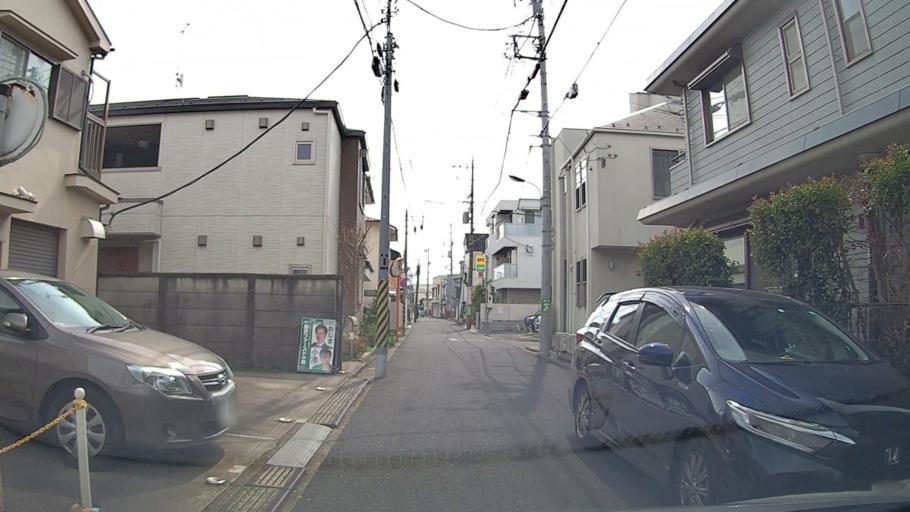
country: JP
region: Saitama
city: Wako
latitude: 35.7455
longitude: 139.6556
